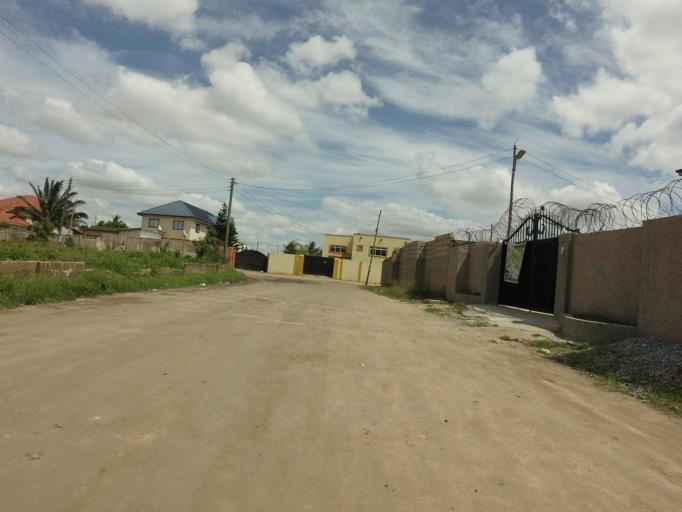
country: GH
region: Central
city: Kasoa
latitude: 5.5442
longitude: -0.4019
